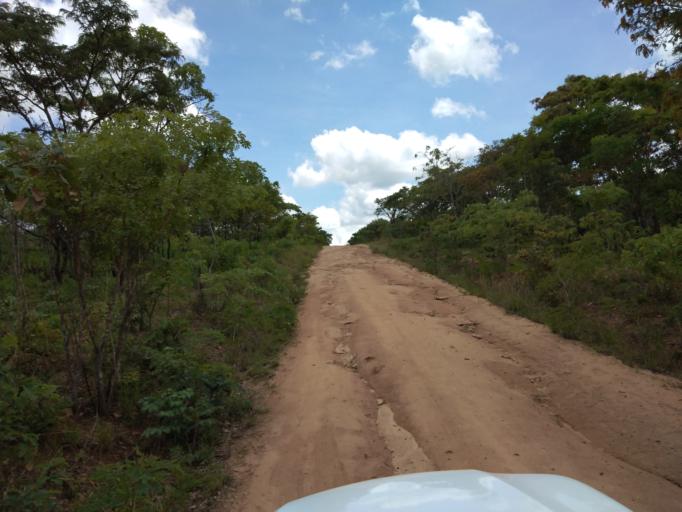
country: ZM
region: Central
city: Mkushi
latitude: -13.9035
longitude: 29.8635
